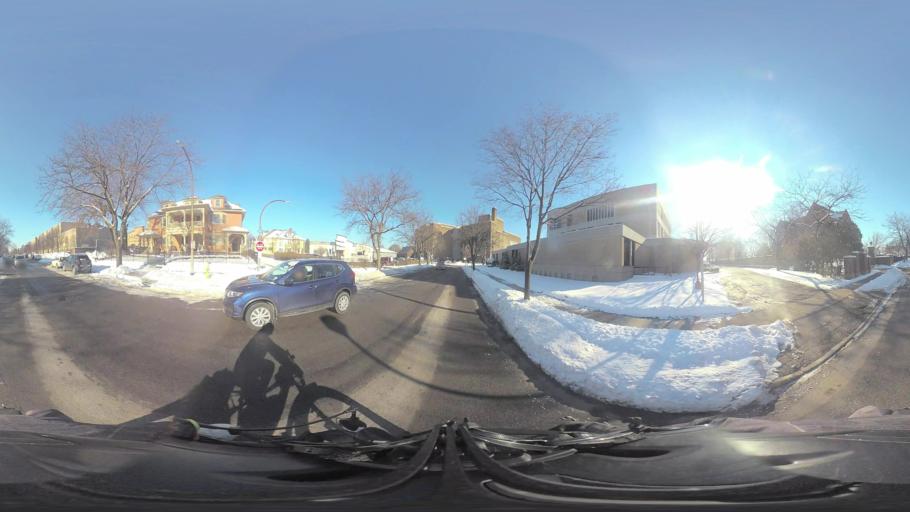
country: US
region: New York
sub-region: Monroe County
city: Rochester
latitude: 43.1587
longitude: -77.5894
